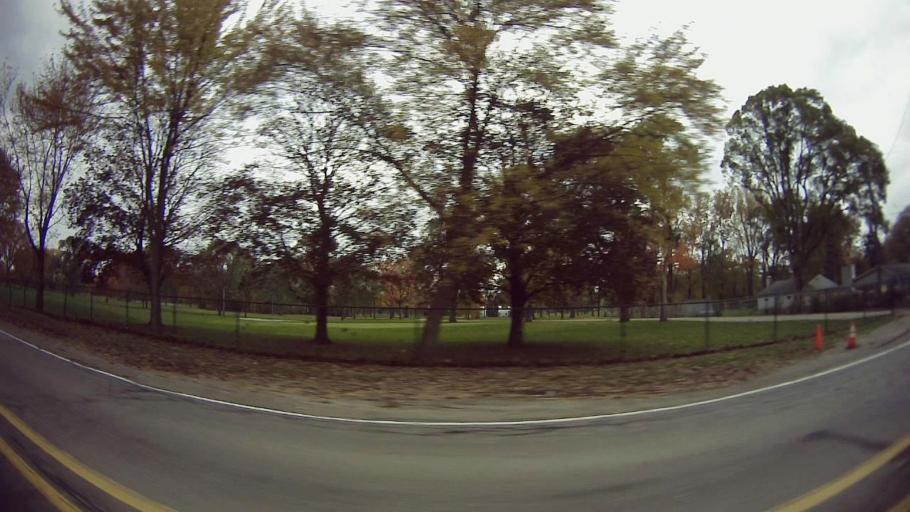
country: US
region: Michigan
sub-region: Macomb County
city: Sterling Heights
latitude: 42.5444
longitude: -83.0042
